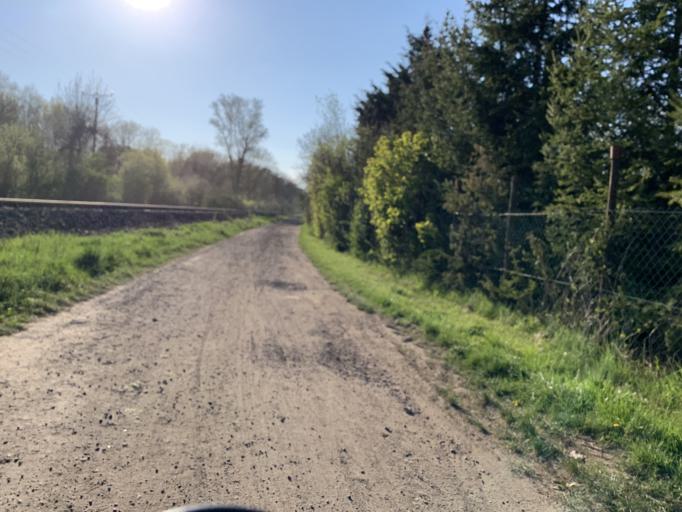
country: DE
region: Rheinland-Pfalz
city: Langenlonsheim
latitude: 49.8901
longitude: 7.8904
